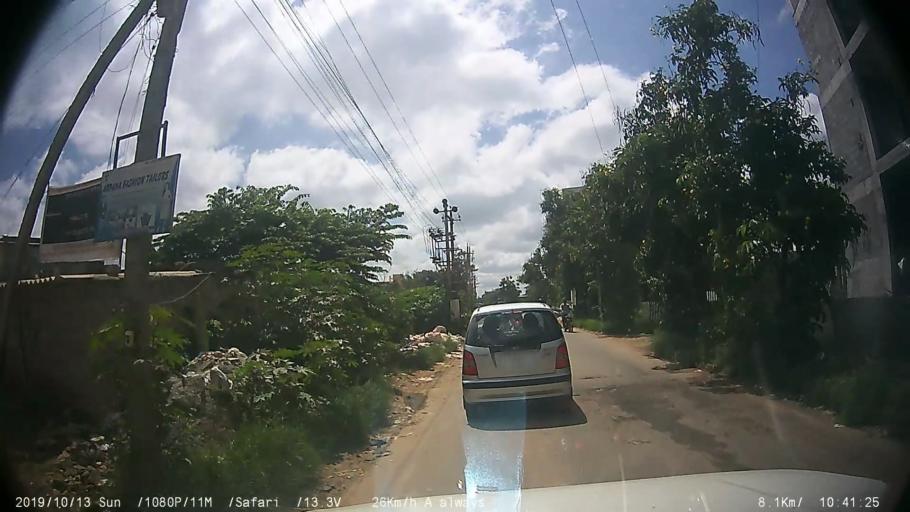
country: IN
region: Karnataka
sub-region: Bangalore Urban
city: Anekal
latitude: 12.8262
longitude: 77.6497
